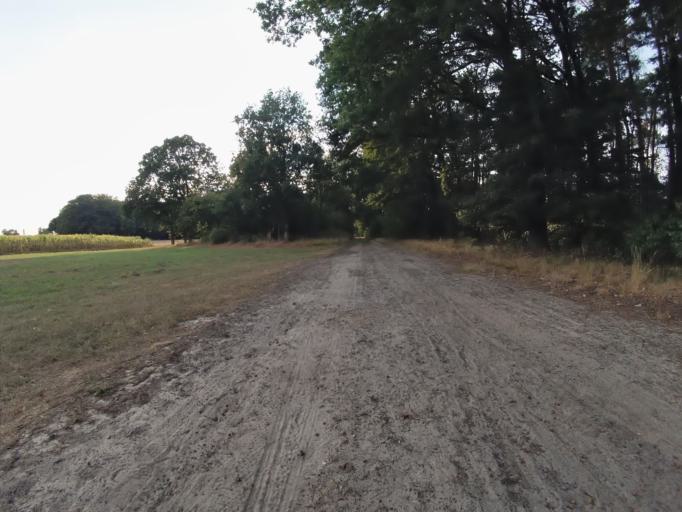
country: DE
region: North Rhine-Westphalia
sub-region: Regierungsbezirk Munster
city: Westerkappeln
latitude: 52.3709
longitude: 7.8837
